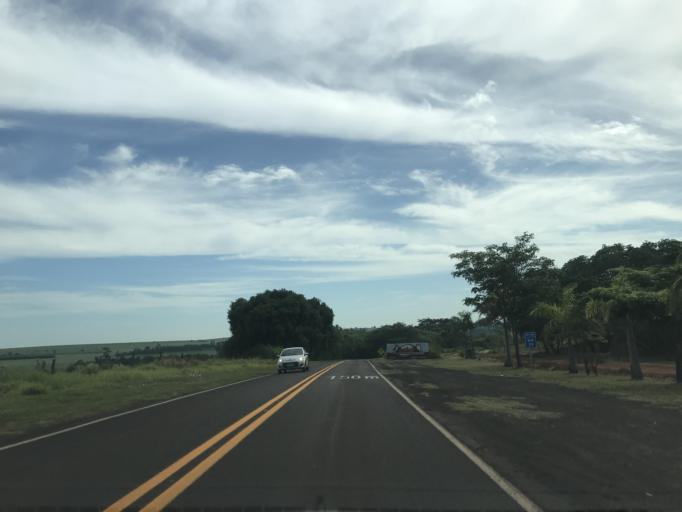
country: BR
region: Parana
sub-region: Terra Rica
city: Terra Rica
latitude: -22.7788
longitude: -52.6567
